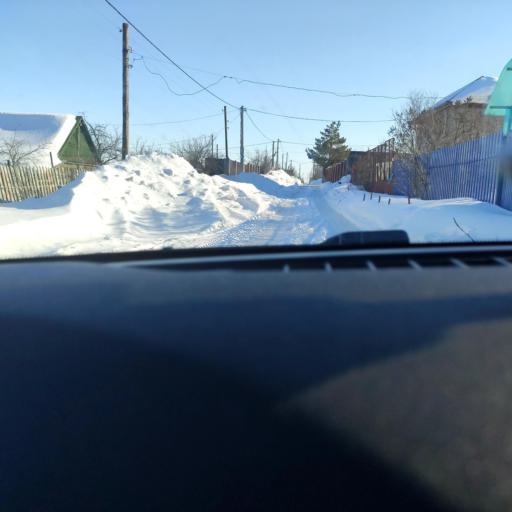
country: RU
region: Samara
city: Petra-Dubrava
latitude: 53.2873
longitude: 50.3070
